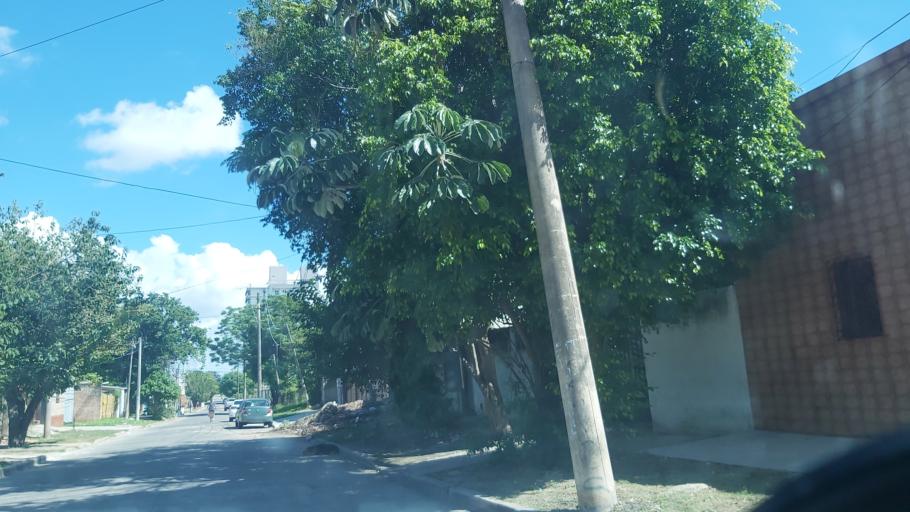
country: AR
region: Corrientes
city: Corrientes
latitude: -27.4765
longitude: -58.8499
